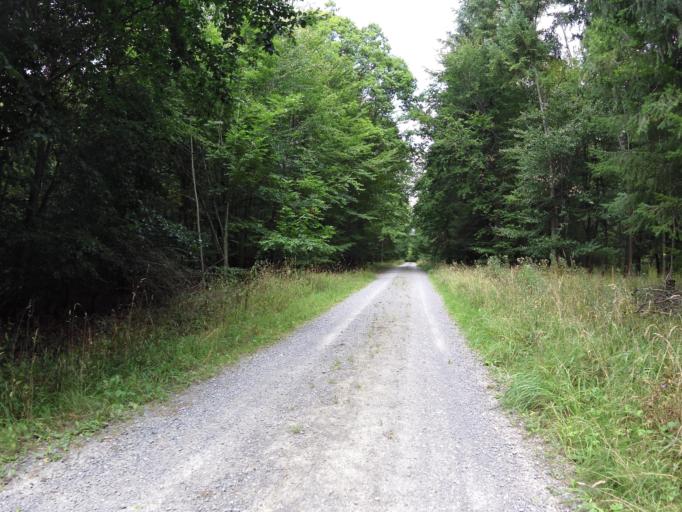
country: DE
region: Bavaria
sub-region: Regierungsbezirk Unterfranken
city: Kleinrinderfeld
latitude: 49.7168
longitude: 9.8155
